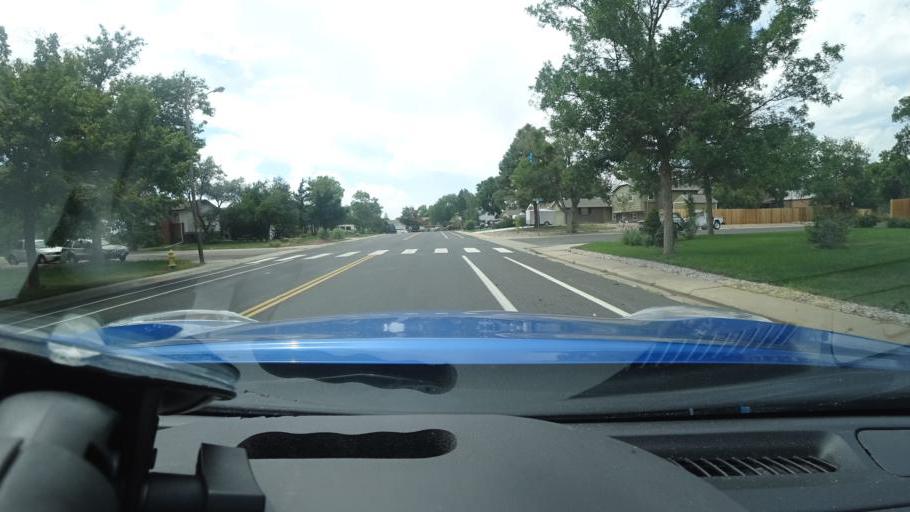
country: US
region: Colorado
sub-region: Adams County
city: Aurora
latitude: 39.7197
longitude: -104.8330
